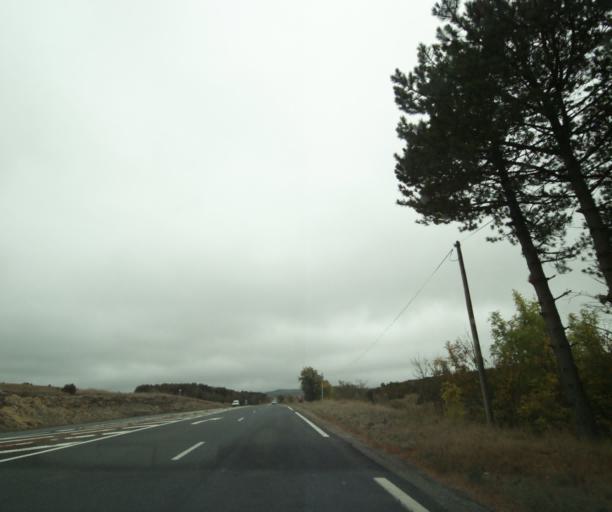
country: FR
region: Midi-Pyrenees
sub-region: Departement de l'Aveyron
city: La Cavalerie
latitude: 44.0341
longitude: 3.1472
